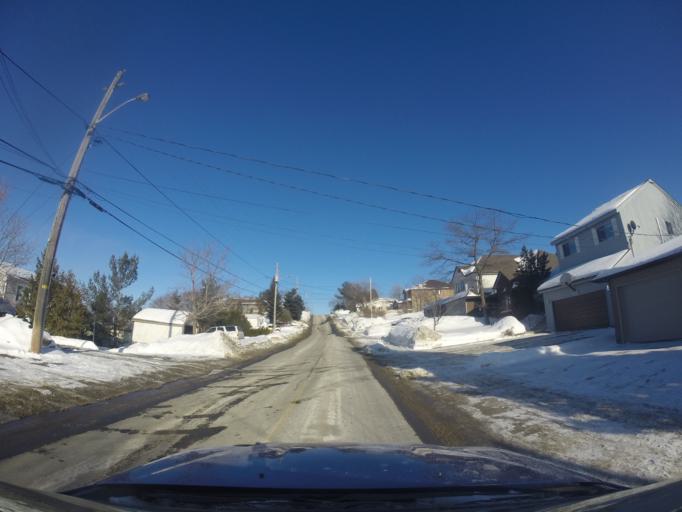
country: CA
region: Ontario
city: Greater Sudbury
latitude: 46.4566
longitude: -80.9963
